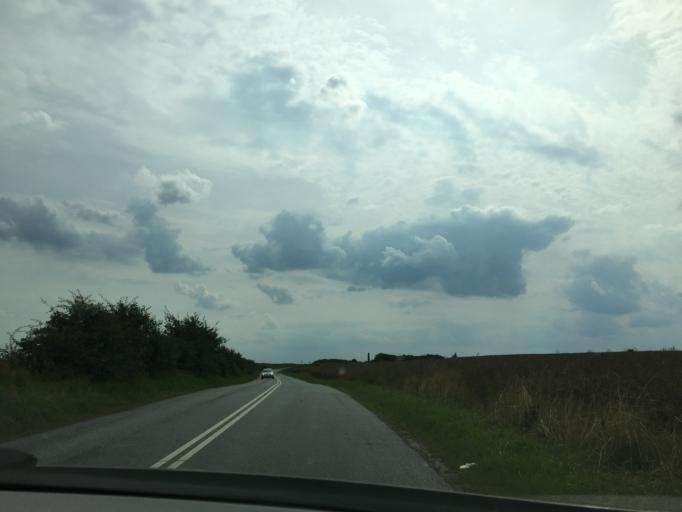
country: DK
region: Central Jutland
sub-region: Viborg Kommune
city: Stoholm
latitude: 56.4683
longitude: 9.1452
